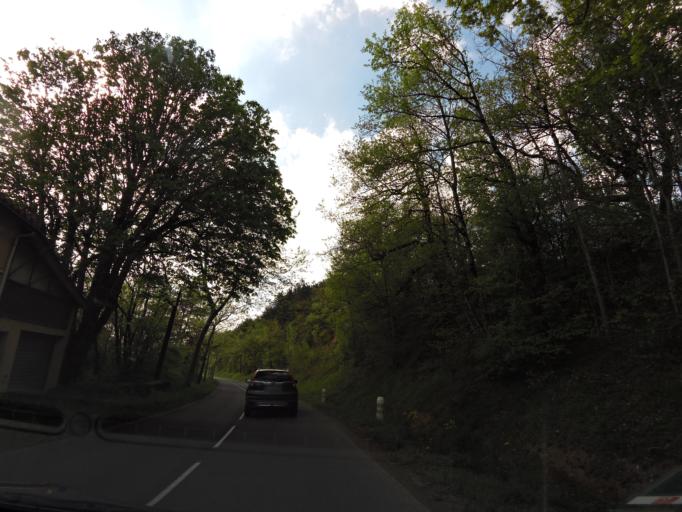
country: FR
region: Midi-Pyrenees
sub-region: Departement du Tarn
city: Soreze
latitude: 43.4350
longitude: 2.0477
